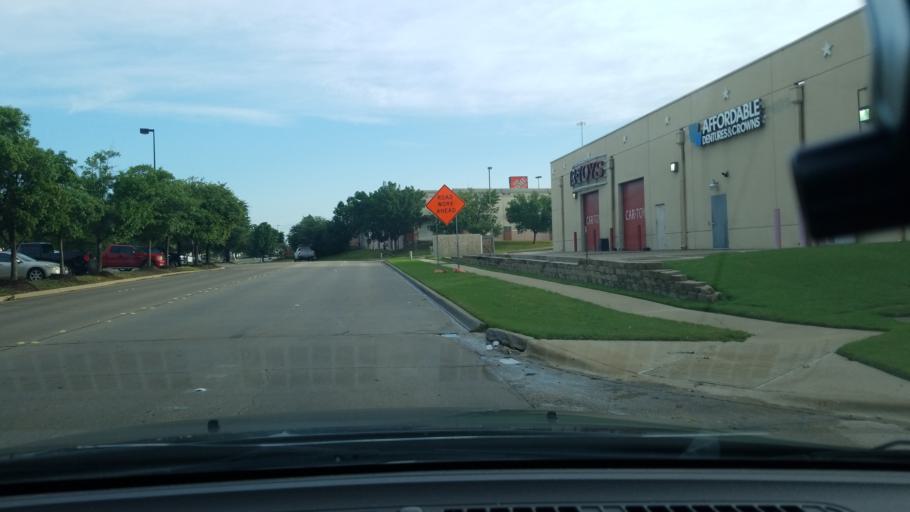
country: US
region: Texas
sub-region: Dallas County
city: Mesquite
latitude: 32.7997
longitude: -96.6276
